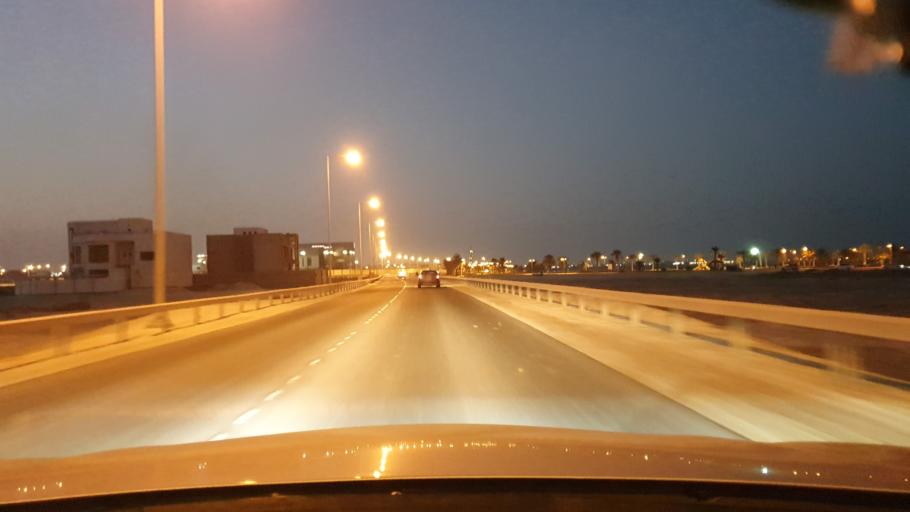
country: BH
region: Northern
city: Ar Rifa'
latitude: 26.0419
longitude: 50.6212
